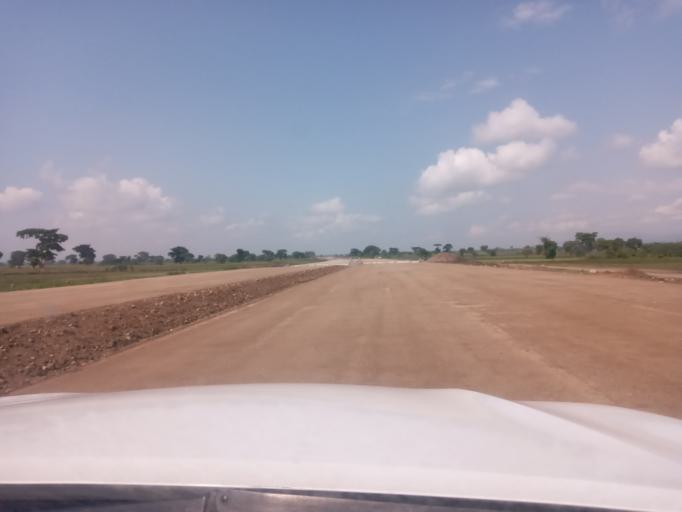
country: ET
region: Oromiya
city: Shashemene
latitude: 7.3042
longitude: 38.6184
